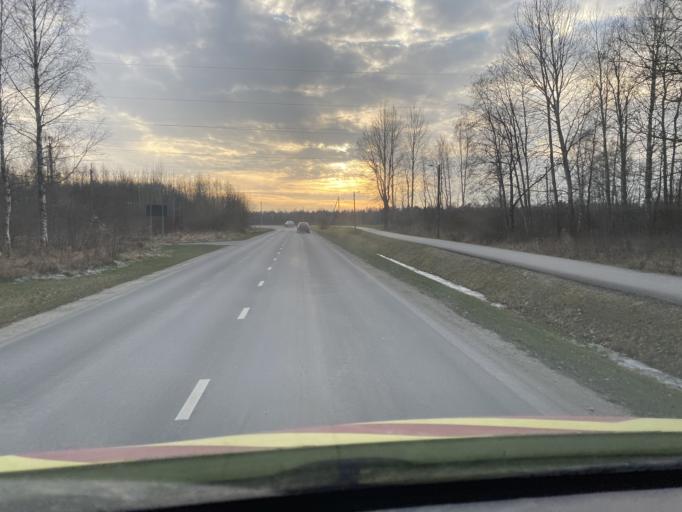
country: EE
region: Jogevamaa
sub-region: Poltsamaa linn
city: Poltsamaa
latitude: 58.6397
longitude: 25.9768
